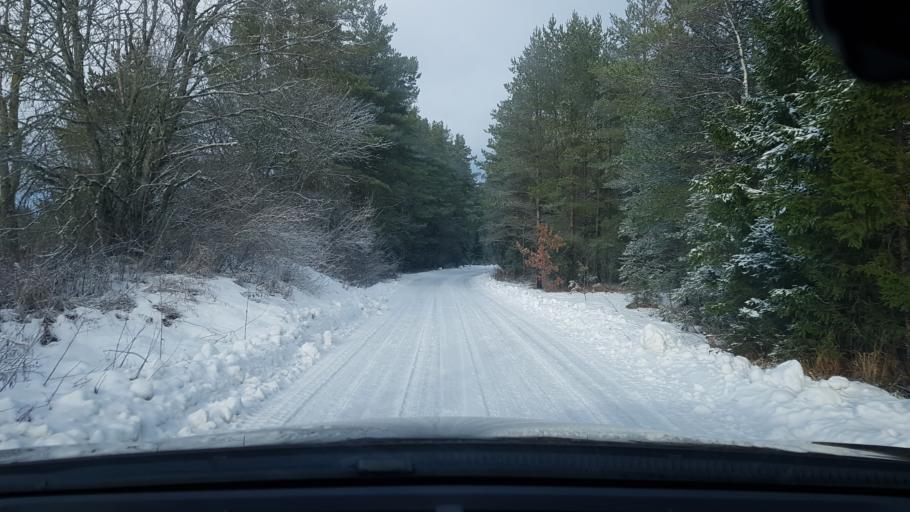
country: EE
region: Harju
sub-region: Keila linn
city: Keila
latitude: 59.2845
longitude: 24.2599
